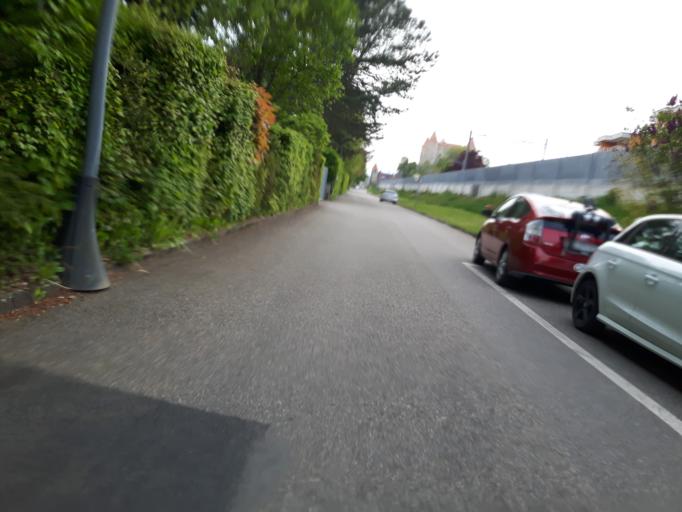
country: CH
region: Vaud
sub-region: Jura-Nord vaudois District
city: Grandson
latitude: 46.8118
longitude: 6.6516
